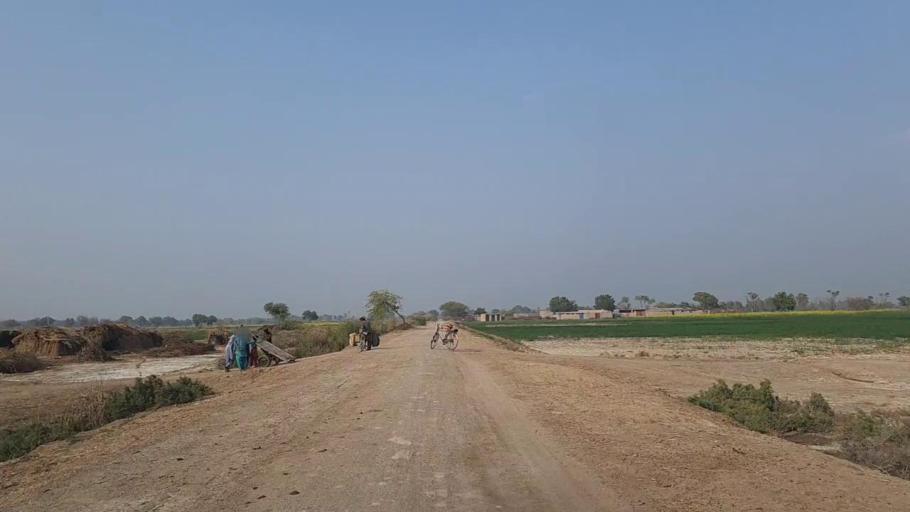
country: PK
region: Sindh
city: Nawabshah
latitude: 26.3474
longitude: 68.4740
